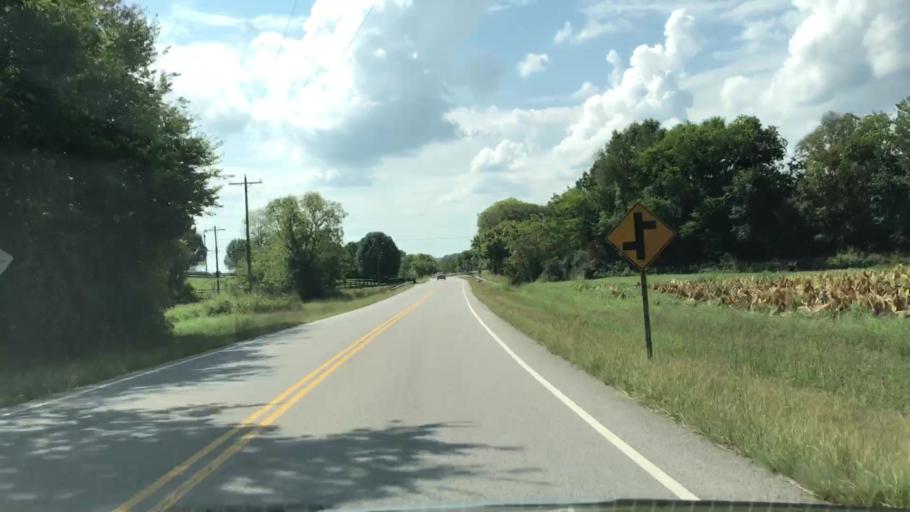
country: US
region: Tennessee
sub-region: Trousdale County
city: Hartsville
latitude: 36.4248
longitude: -86.1831
